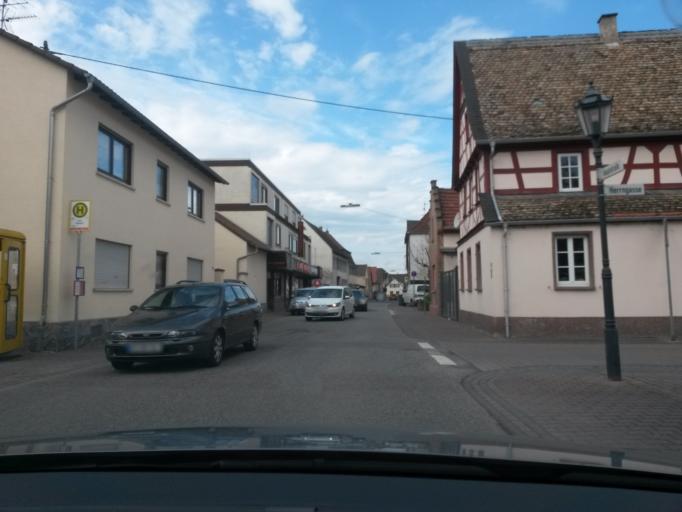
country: DE
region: Rheinland-Pfalz
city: Eich
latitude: 49.7498
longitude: 8.4022
